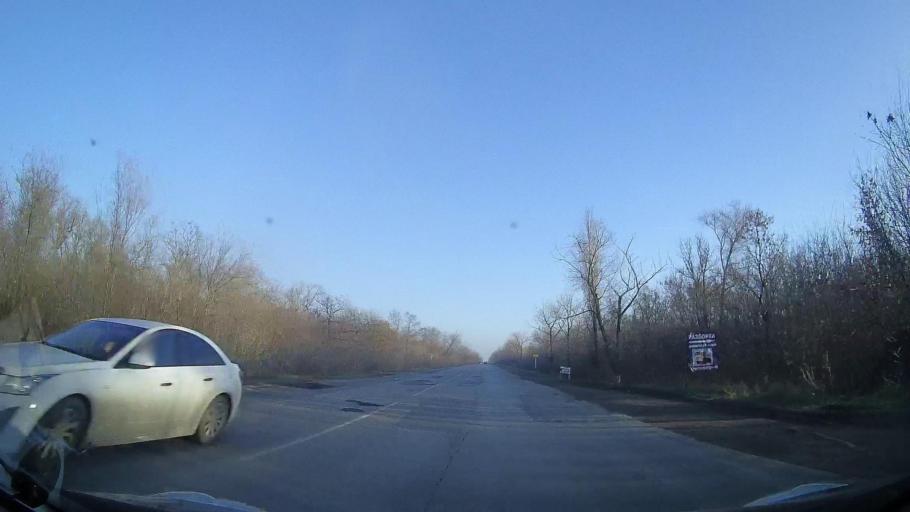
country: RU
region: Rostov
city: Bataysk
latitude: 47.0455
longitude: 39.8479
